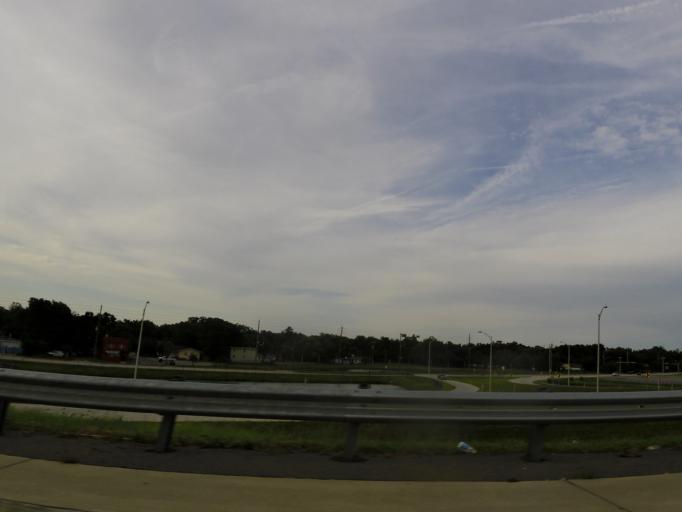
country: US
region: Florida
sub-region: Duval County
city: Jacksonville
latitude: 30.3561
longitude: -81.6384
